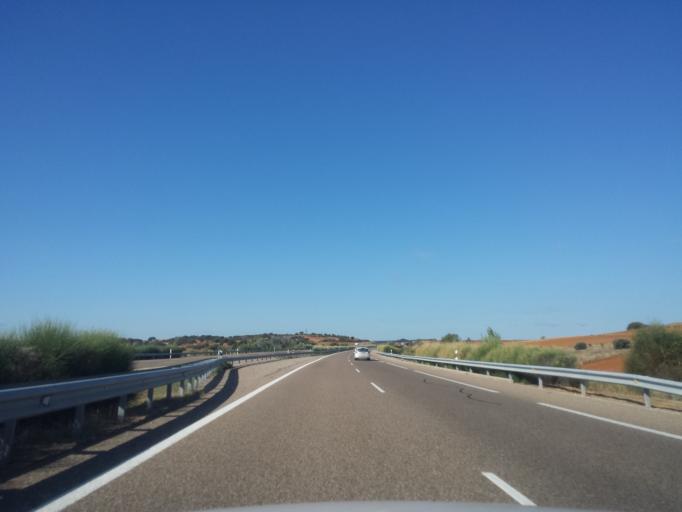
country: ES
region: Castille and Leon
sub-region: Provincia de Leon
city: Villamandos
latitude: 42.1922
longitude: -5.6103
